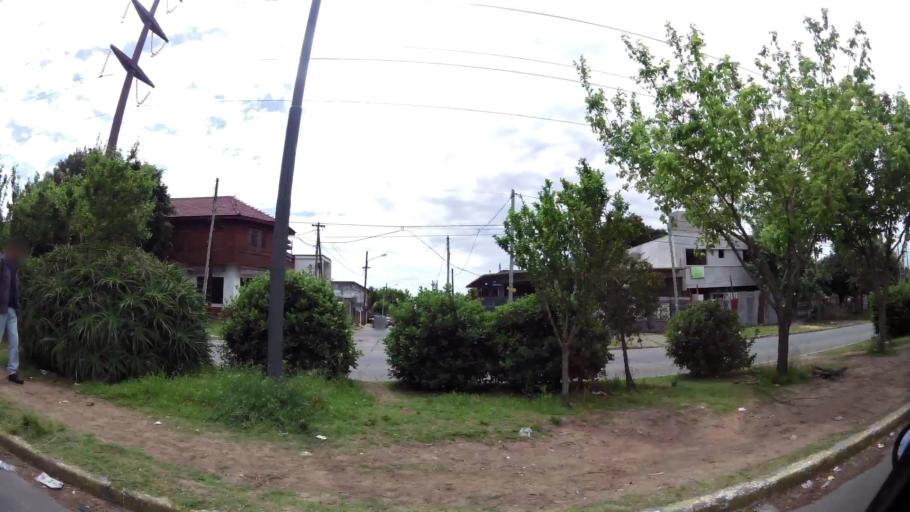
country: AR
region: Buenos Aires
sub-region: Partido de Quilmes
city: Quilmes
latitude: -34.7608
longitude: -58.2355
